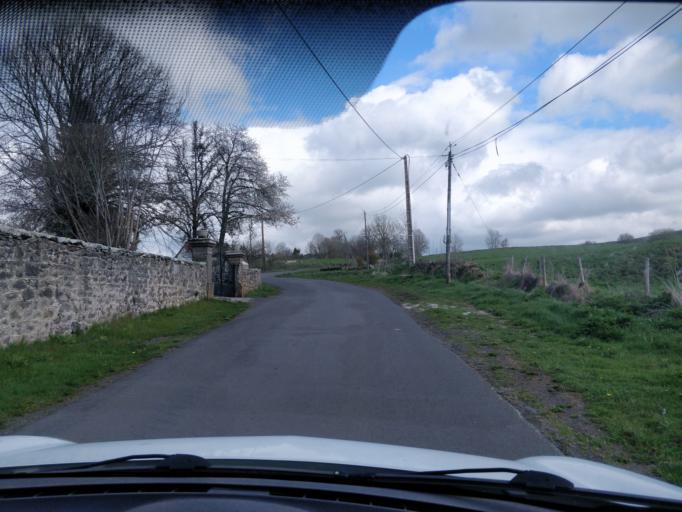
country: FR
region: Auvergne
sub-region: Departement du Cantal
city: Allanche
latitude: 45.2124
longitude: 2.9425
